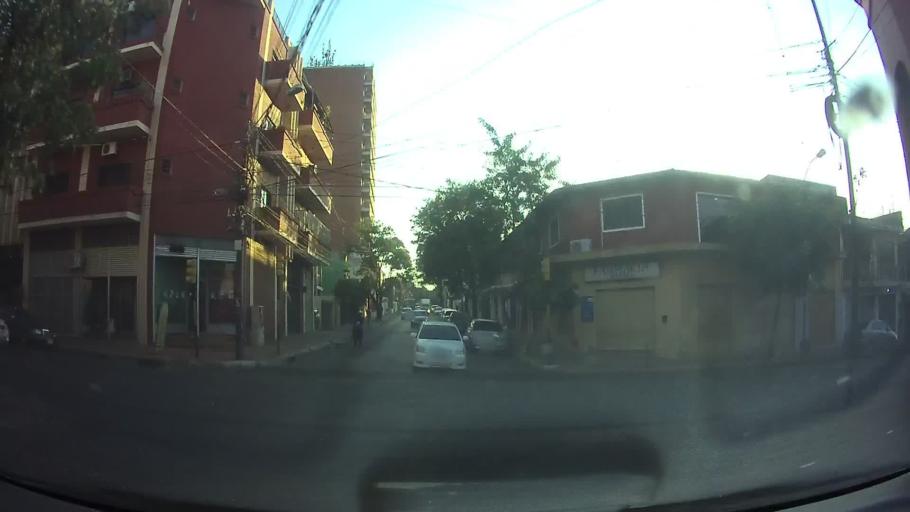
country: PY
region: Asuncion
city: Asuncion
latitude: -25.2939
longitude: -57.6285
